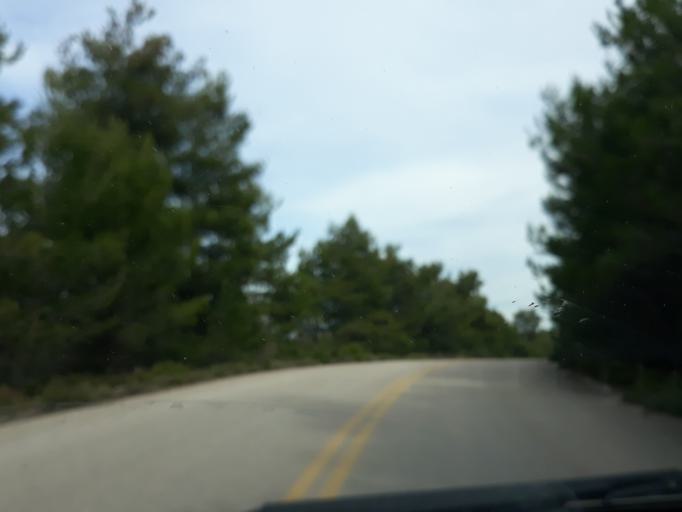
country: GR
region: Attica
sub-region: Nomarchia Anatolikis Attikis
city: Afidnes
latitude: 38.1914
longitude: 23.7897
